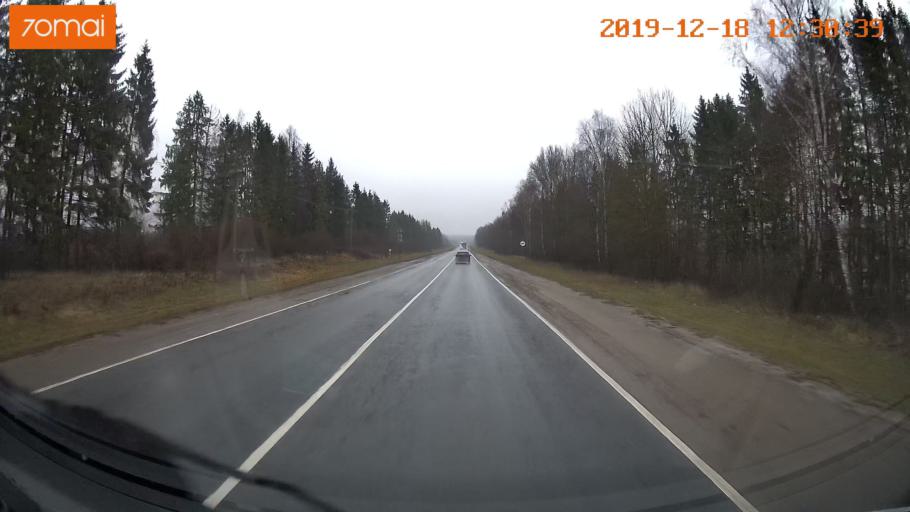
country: RU
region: Moskovskaya
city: Novopetrovskoye
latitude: 56.0917
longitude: 36.5348
